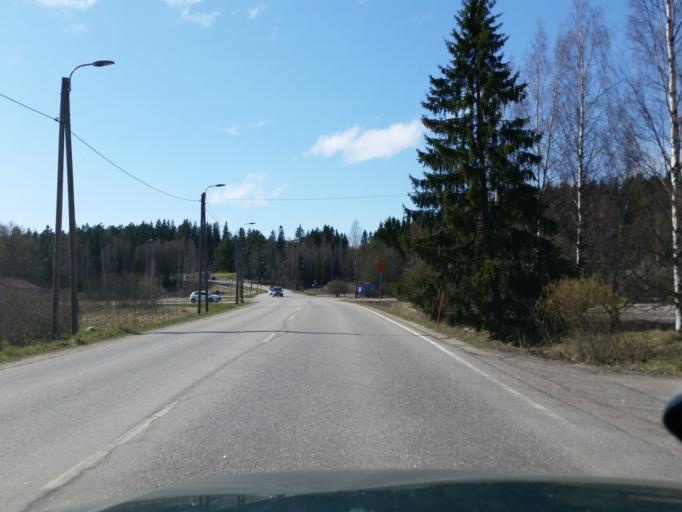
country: FI
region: Uusimaa
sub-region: Helsinki
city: Vihti
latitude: 60.4219
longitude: 24.3094
